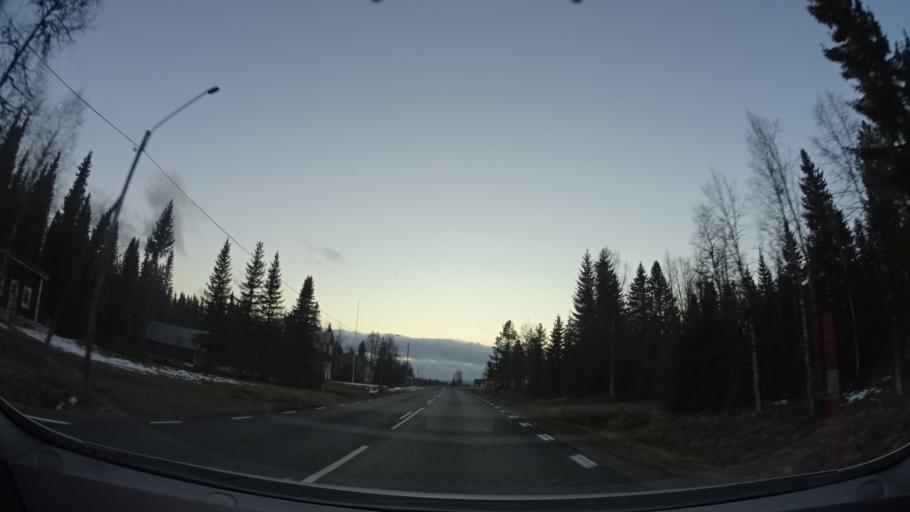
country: SE
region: Vaesterbotten
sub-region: Lycksele Kommun
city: Soderfors
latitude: 64.4258
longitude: 18.0631
